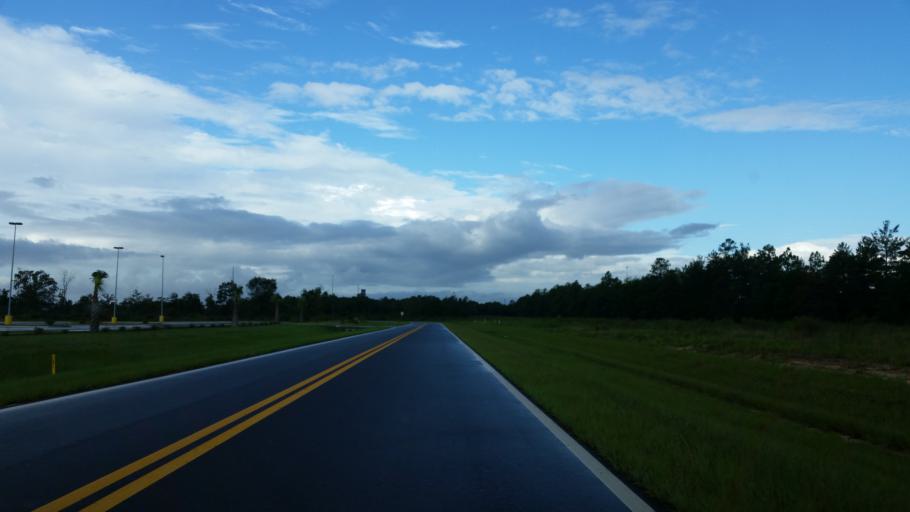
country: US
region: Florida
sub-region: Walton County
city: DeFuniak Springs
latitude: 30.7371
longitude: -86.3424
